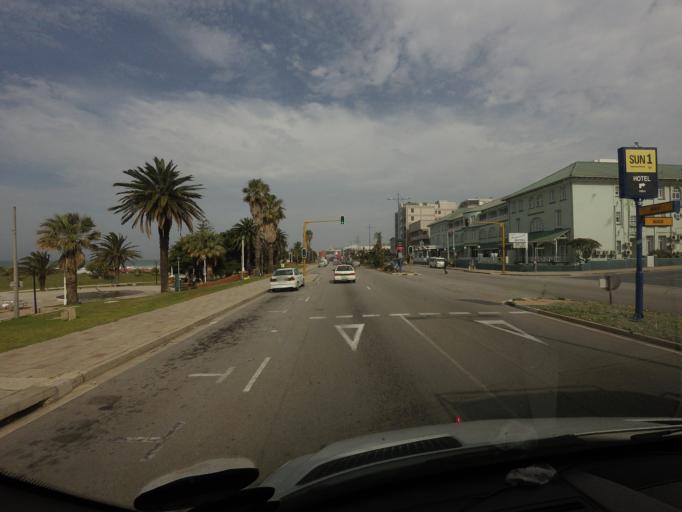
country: ZA
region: Eastern Cape
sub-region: Nelson Mandela Bay Metropolitan Municipality
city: Port Elizabeth
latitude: -33.9755
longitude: 25.6460
